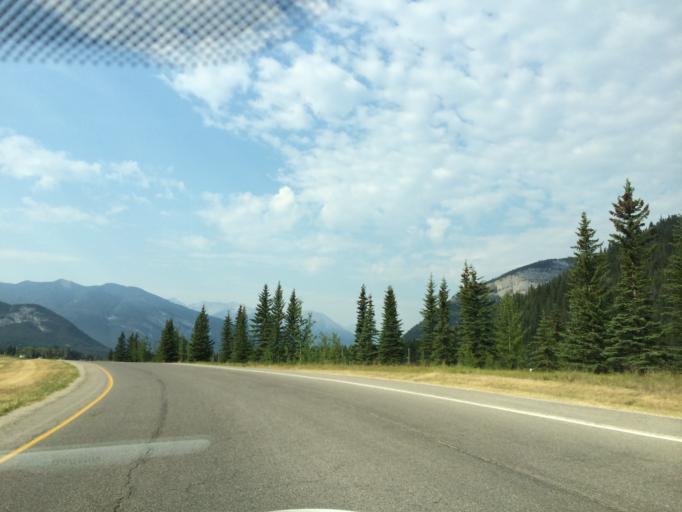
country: CA
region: Alberta
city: Banff
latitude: 51.2089
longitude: -115.5385
